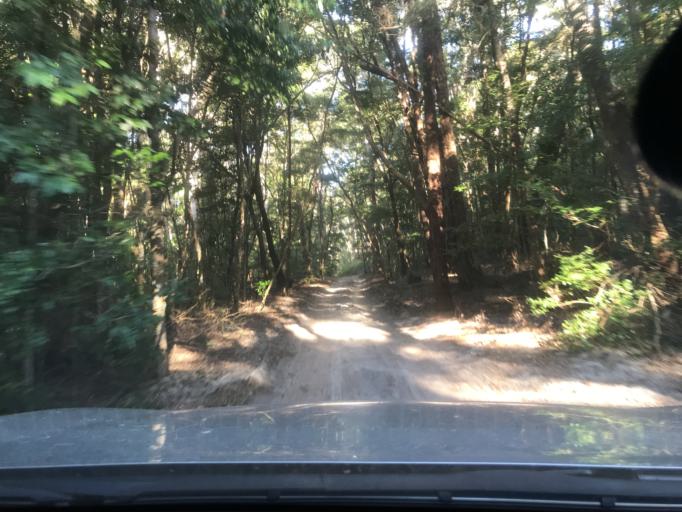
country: AU
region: Queensland
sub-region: Fraser Coast
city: Urangan
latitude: -25.3262
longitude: 153.1507
